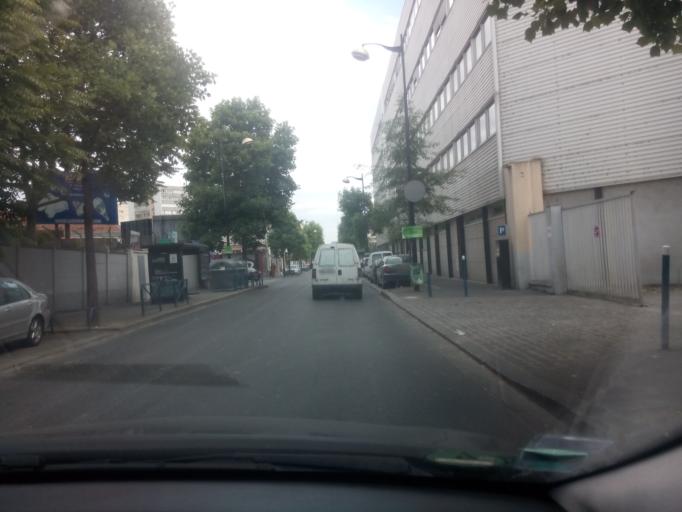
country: FR
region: Ile-de-France
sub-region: Departement de Seine-Saint-Denis
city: Aubervilliers
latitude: 48.9067
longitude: 2.3796
